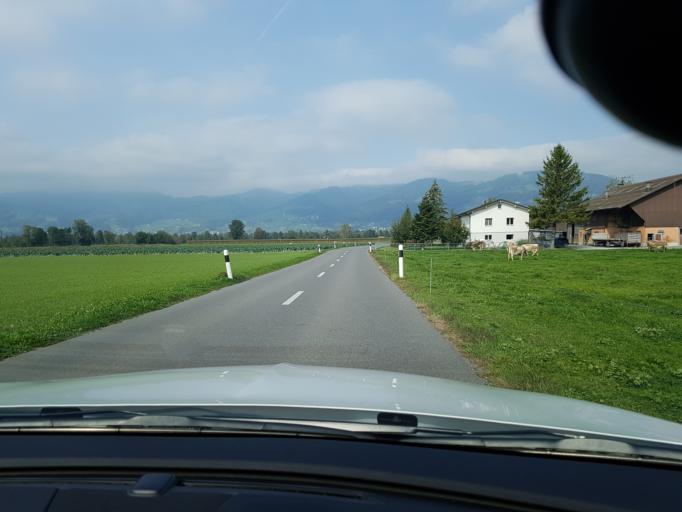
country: AT
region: Vorarlberg
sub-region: Politischer Bezirk Feldkirch
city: Mader
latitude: 47.3698
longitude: 9.6079
